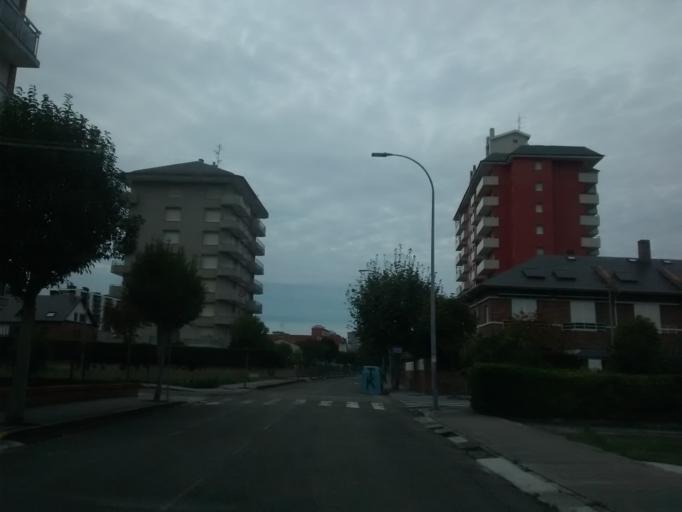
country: ES
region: Cantabria
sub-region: Provincia de Cantabria
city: Colindres
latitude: 43.4207
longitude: -3.4448
